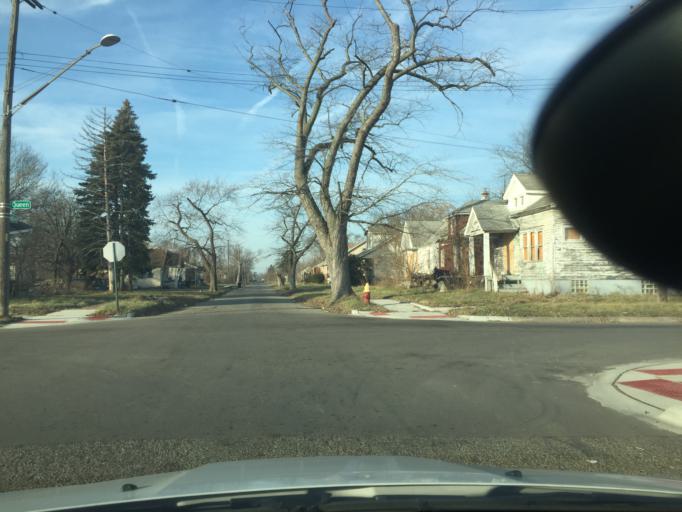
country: US
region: Michigan
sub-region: Macomb County
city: Eastpointe
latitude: 42.4345
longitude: -82.9678
